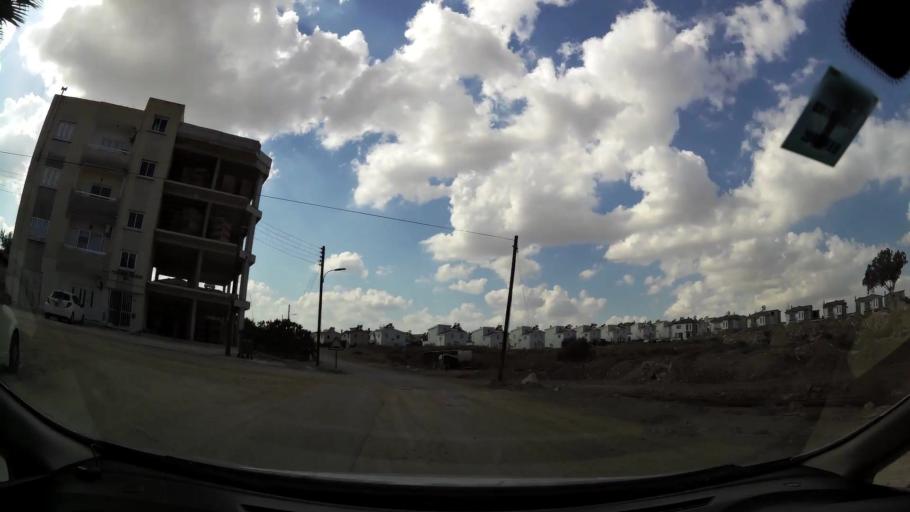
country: CY
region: Lefkosia
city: Nicosia
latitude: 35.2205
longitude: 33.3739
